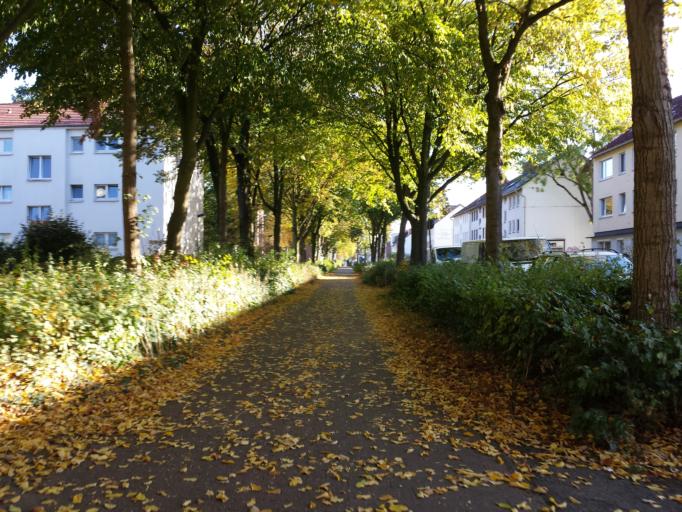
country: DE
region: Bremen
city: Bremen
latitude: 53.0933
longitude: 8.7839
